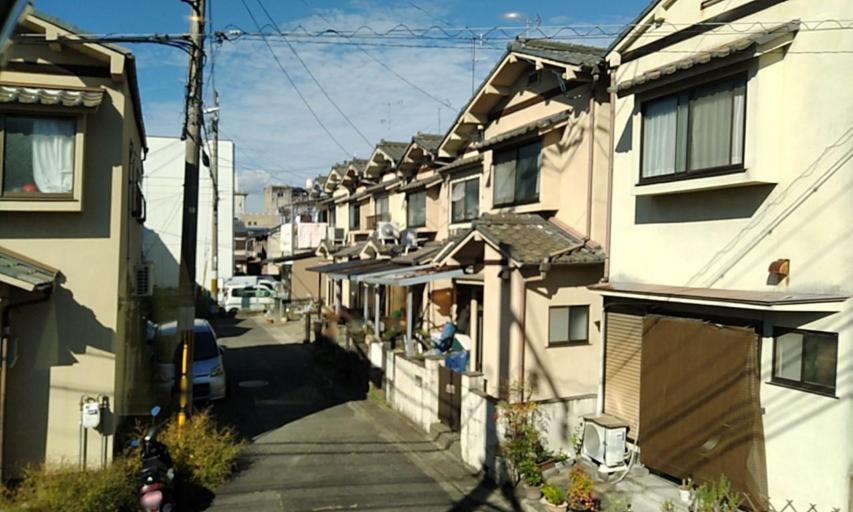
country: JP
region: Kyoto
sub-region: Kyoto-shi
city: Kamigyo-ku
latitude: 35.0456
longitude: 135.7880
